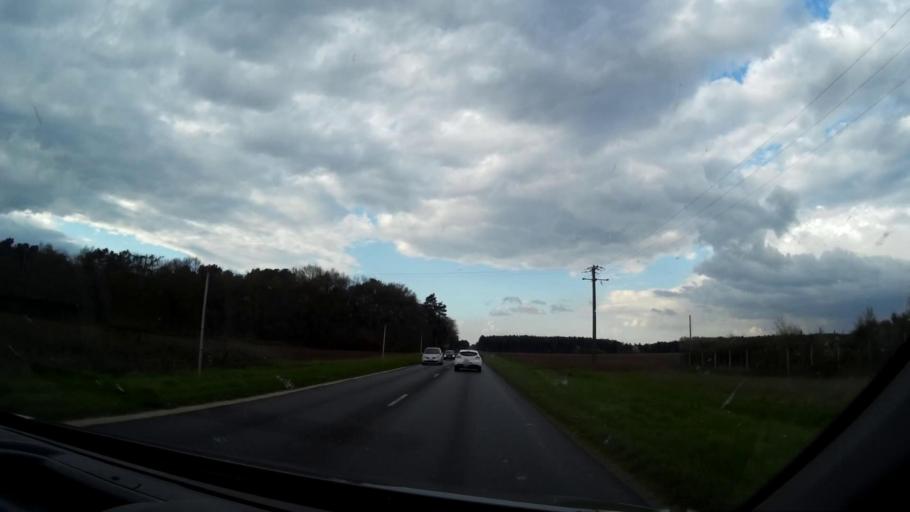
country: FR
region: Centre
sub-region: Departement du Loir-et-Cher
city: Contres
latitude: 47.4493
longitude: 1.4261
